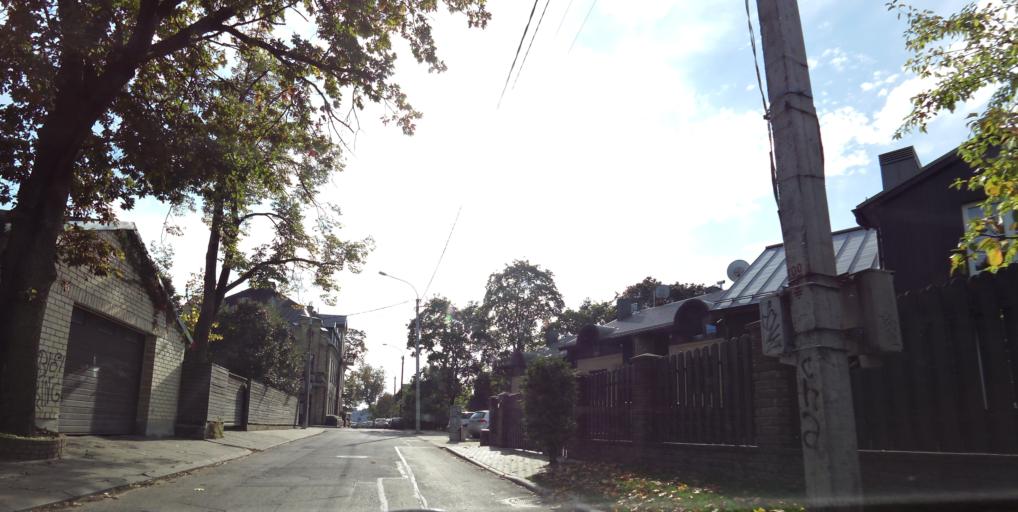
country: LT
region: Vilnius County
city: Seskine
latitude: 54.6939
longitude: 25.2444
